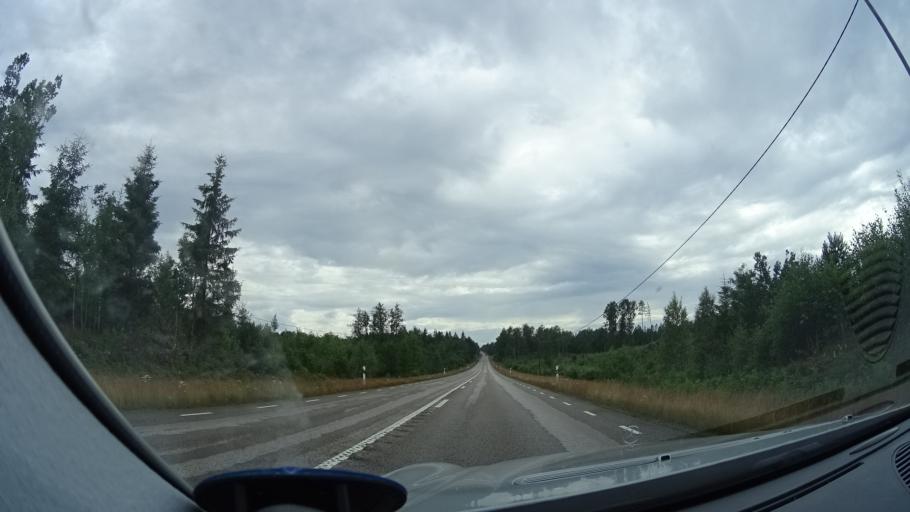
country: SE
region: Kronoberg
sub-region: Tingsryds Kommun
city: Tingsryd
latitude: 56.4454
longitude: 14.9839
